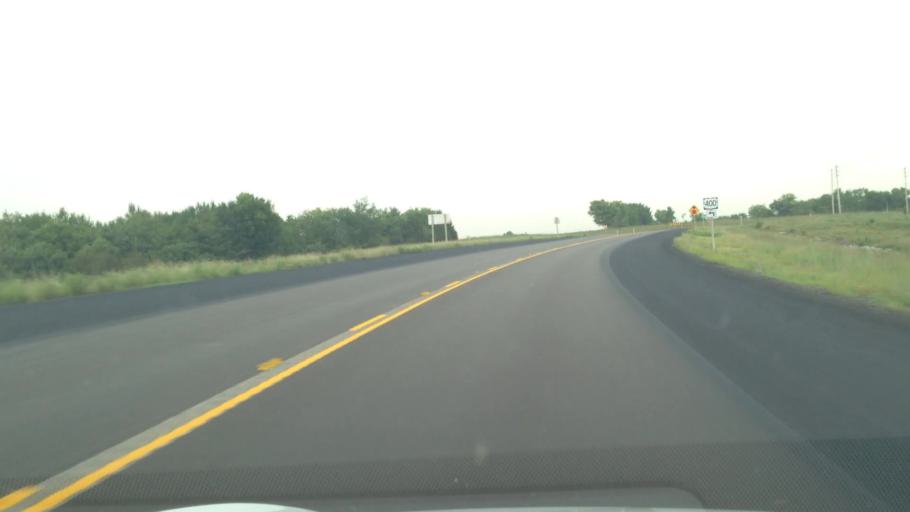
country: US
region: Kansas
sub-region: Cherokee County
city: Baxter Springs
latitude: 37.0263
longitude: -94.7021
